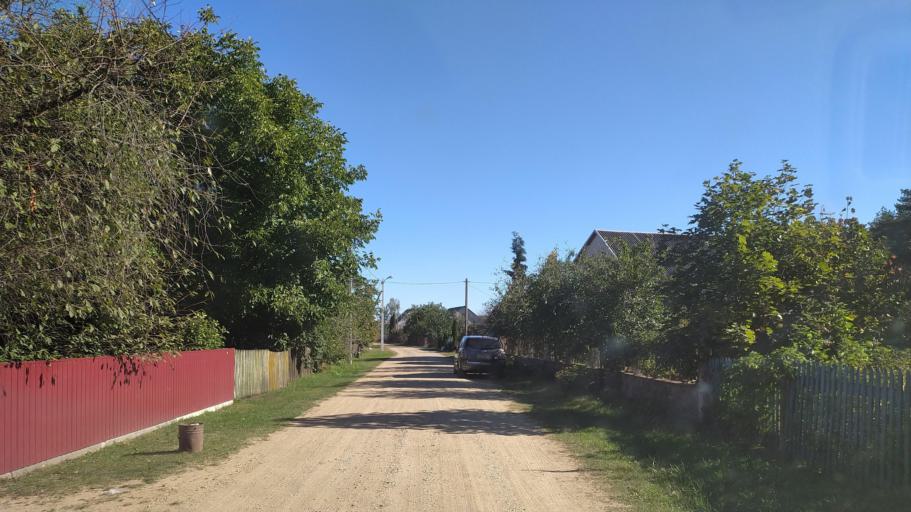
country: BY
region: Brest
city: Pruzhany
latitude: 52.4829
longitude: 24.7079
